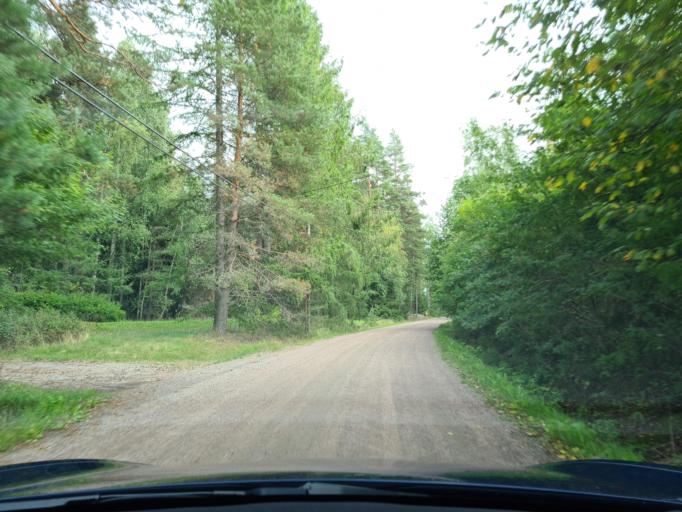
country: FI
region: Uusimaa
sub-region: Helsinki
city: Vihti
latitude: 60.4222
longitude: 24.4761
